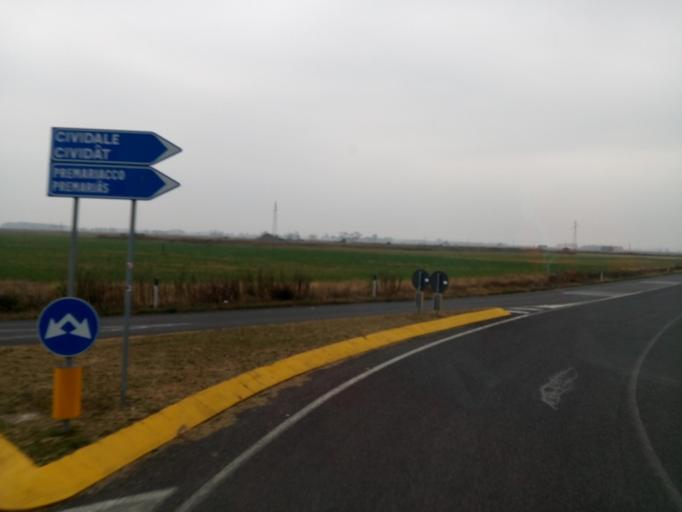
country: IT
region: Friuli Venezia Giulia
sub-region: Provincia di Udine
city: Buttrio
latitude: 46.0417
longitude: 13.3326
